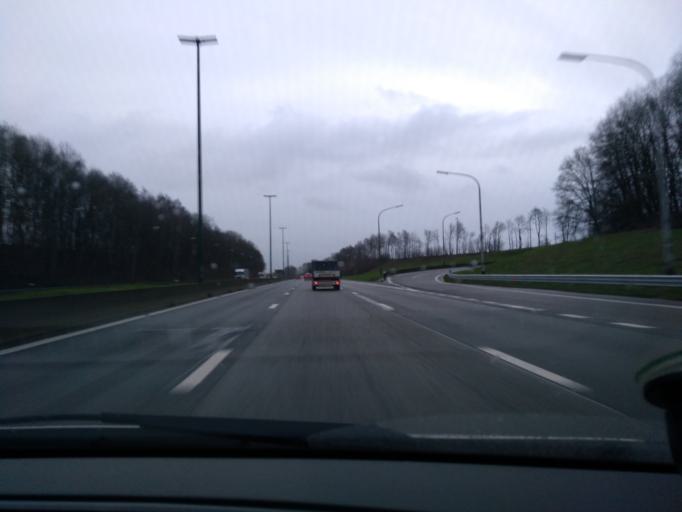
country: BE
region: Wallonia
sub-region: Province du Hainaut
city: Chapelle-lez-Herlaimont
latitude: 50.4855
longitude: 4.2723
